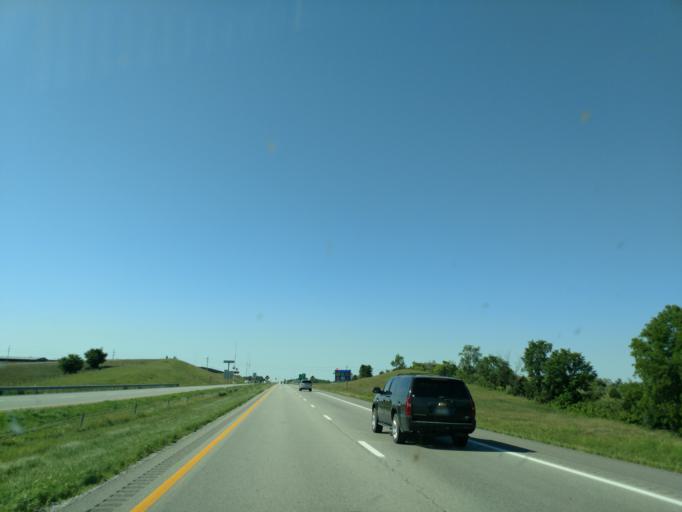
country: US
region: Missouri
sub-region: Buchanan County
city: Saint Joseph
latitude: 39.7149
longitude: -94.7884
